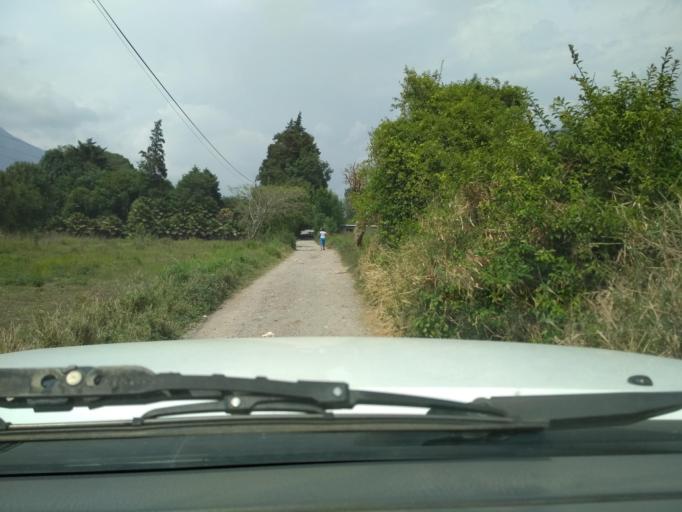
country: MX
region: Veracruz
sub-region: Acultzingo
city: Acatla
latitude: 18.7639
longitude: -97.2212
